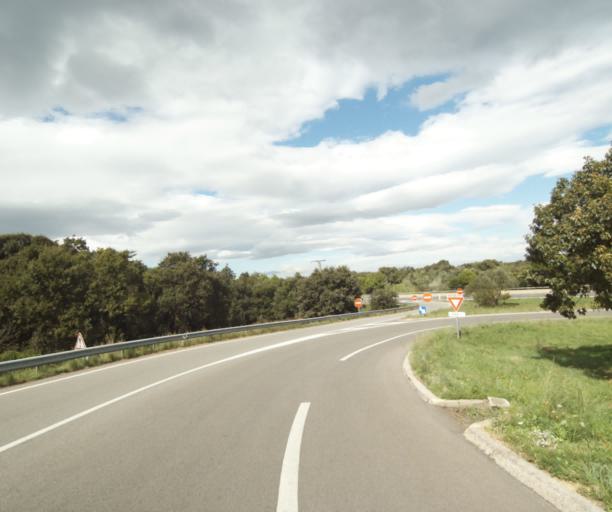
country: FR
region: Languedoc-Roussillon
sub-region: Departement des Pyrenees-Orientales
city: Argelers
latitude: 42.5358
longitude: 3.0314
